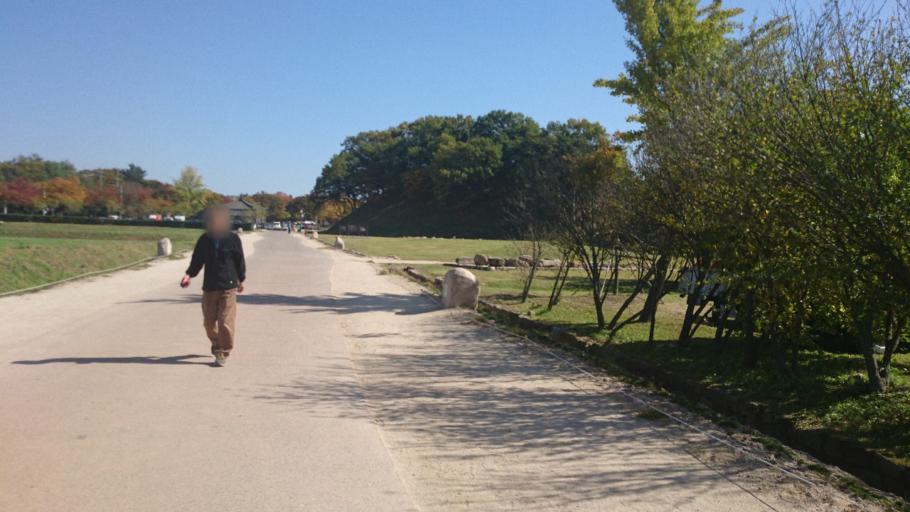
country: KR
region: Gyeongsangbuk-do
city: Kyonju
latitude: 35.8340
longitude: 129.2226
